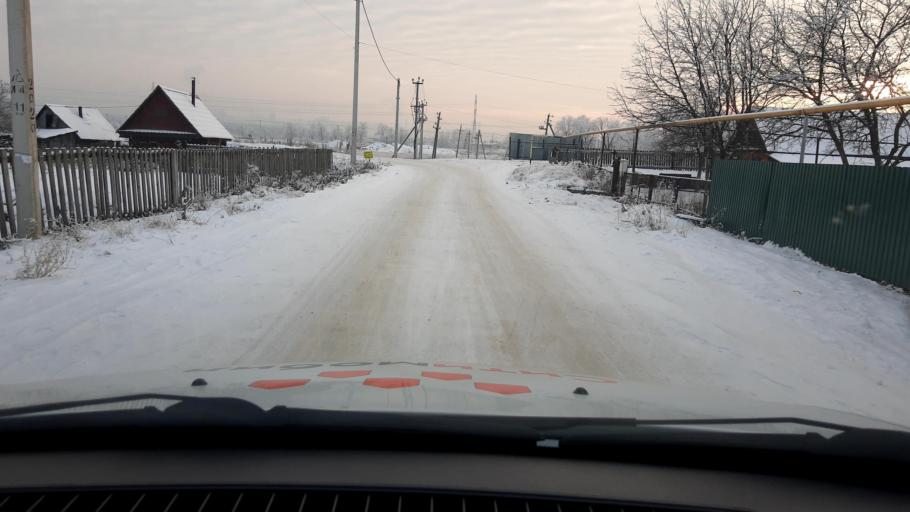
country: RU
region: Bashkortostan
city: Ufa
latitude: 54.7836
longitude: 55.9544
